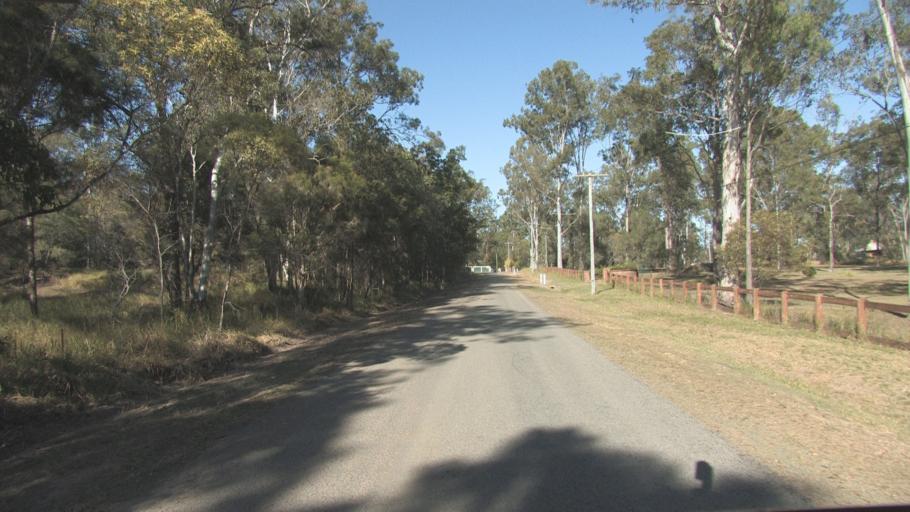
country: AU
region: Queensland
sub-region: Logan
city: Cedar Vale
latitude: -27.8433
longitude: 153.0402
